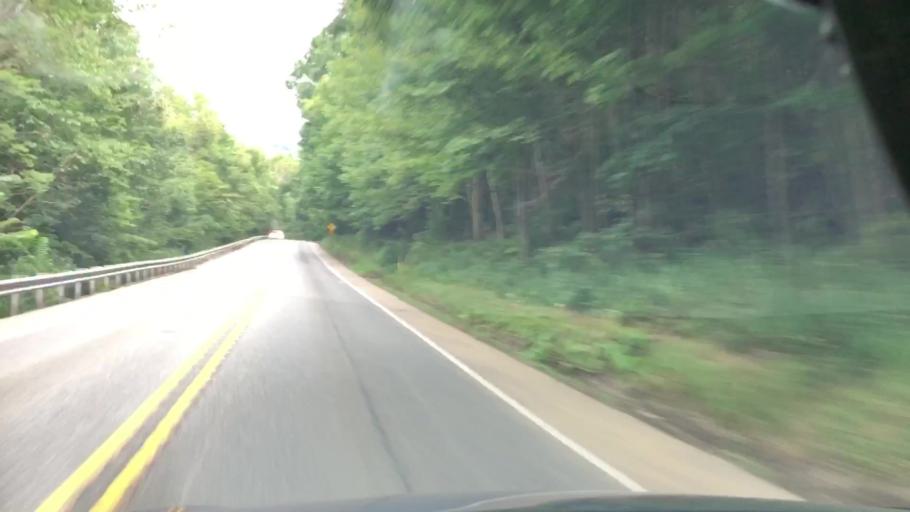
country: US
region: Pennsylvania
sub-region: Venango County
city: Hasson Heights
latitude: 41.5208
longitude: -79.7091
